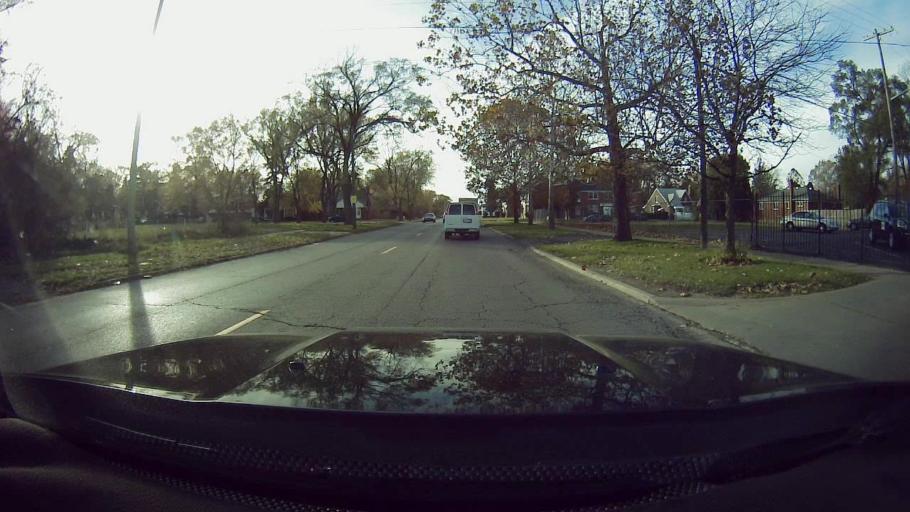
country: US
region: Michigan
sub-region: Oakland County
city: Oak Park
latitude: 42.4087
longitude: -83.2009
